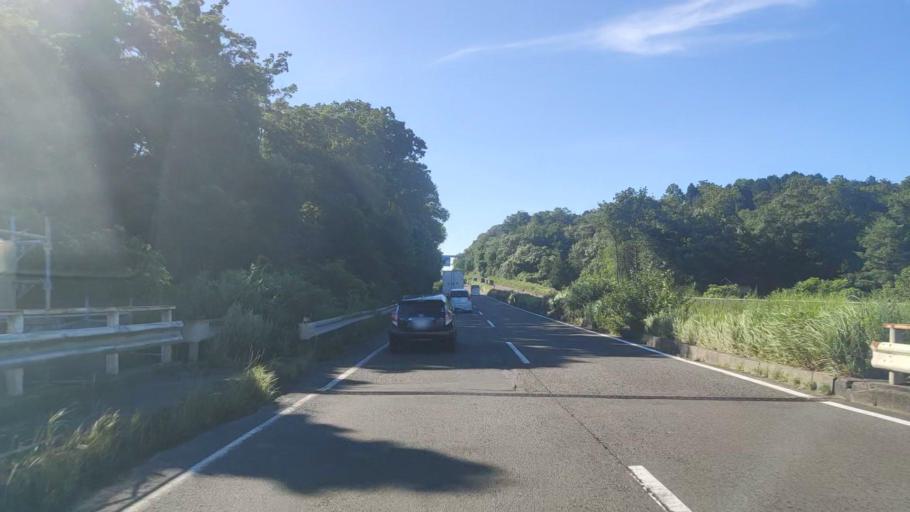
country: JP
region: Shiga Prefecture
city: Minakuchicho-matoba
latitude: 34.9684
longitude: 136.1943
